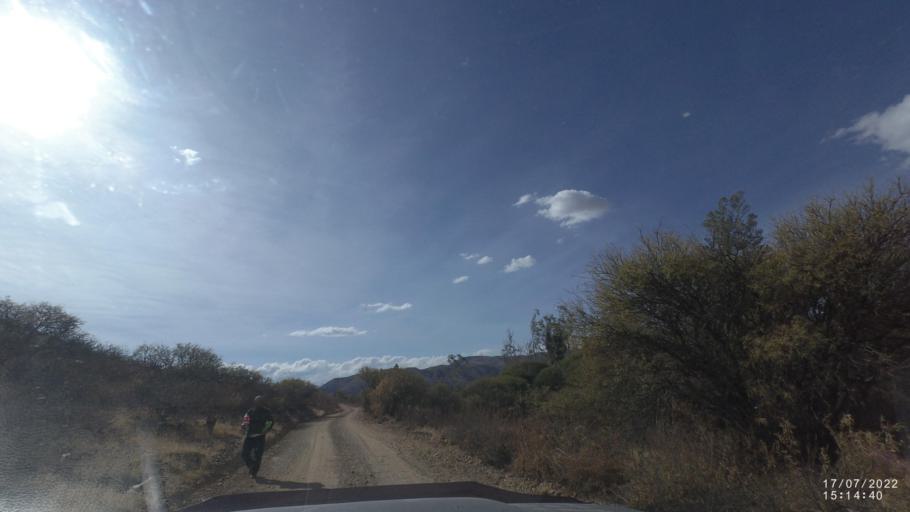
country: BO
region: Cochabamba
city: Capinota
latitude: -17.5610
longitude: -66.2613
